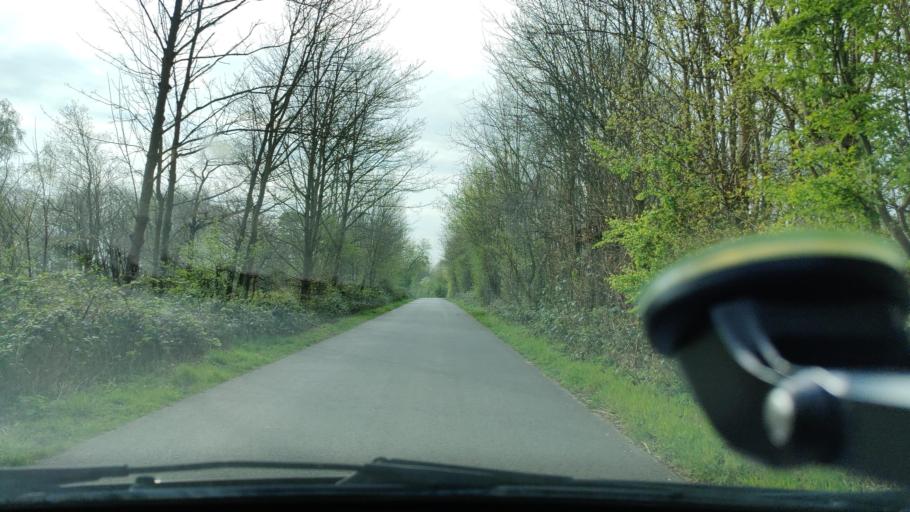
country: DE
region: North Rhine-Westphalia
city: Rheinberg
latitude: 51.5252
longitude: 6.6310
